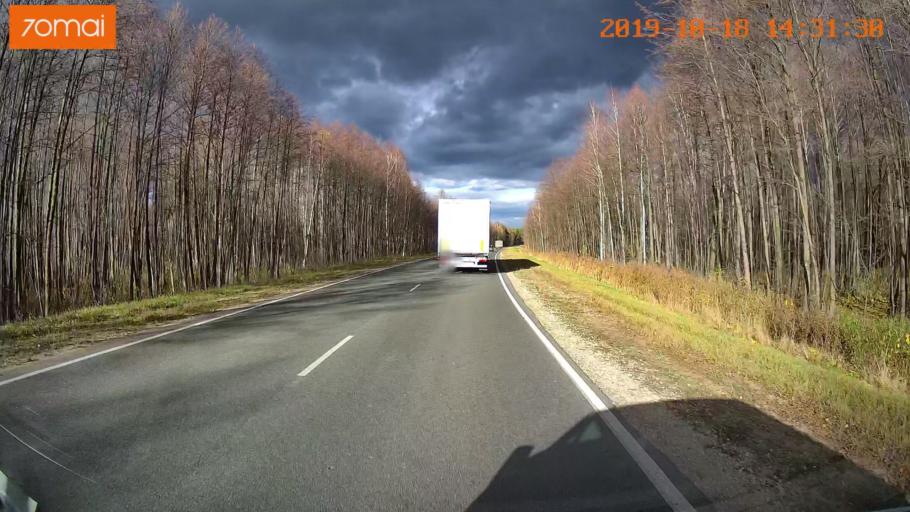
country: RU
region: Rjazan
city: Tuma
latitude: 55.1832
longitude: 40.5703
